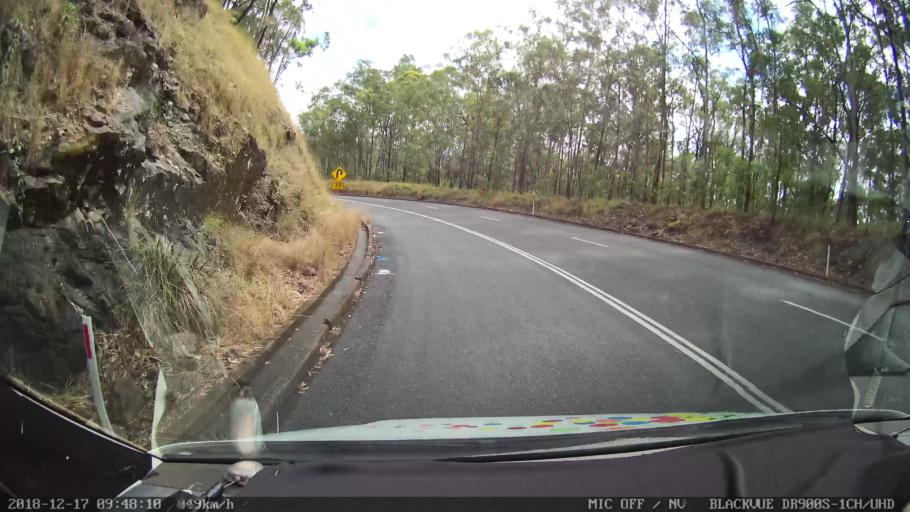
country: AU
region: New South Wales
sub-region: Tenterfield Municipality
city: Carrolls Creek
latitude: -28.9249
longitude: 152.3432
